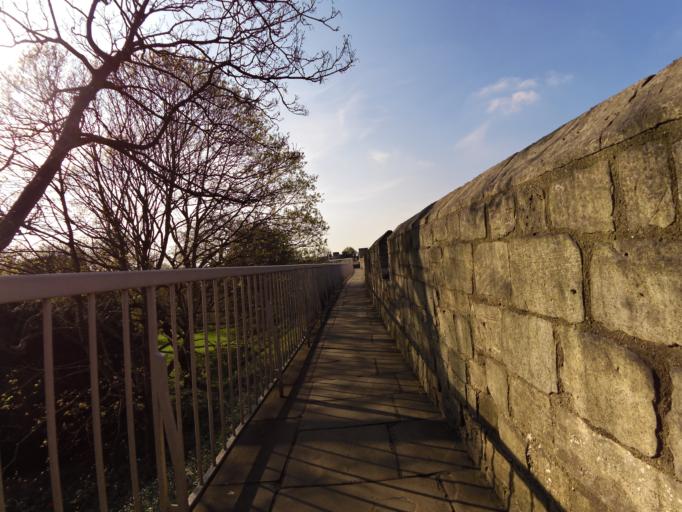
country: GB
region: England
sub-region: City of York
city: York
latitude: 53.9641
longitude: -1.0812
